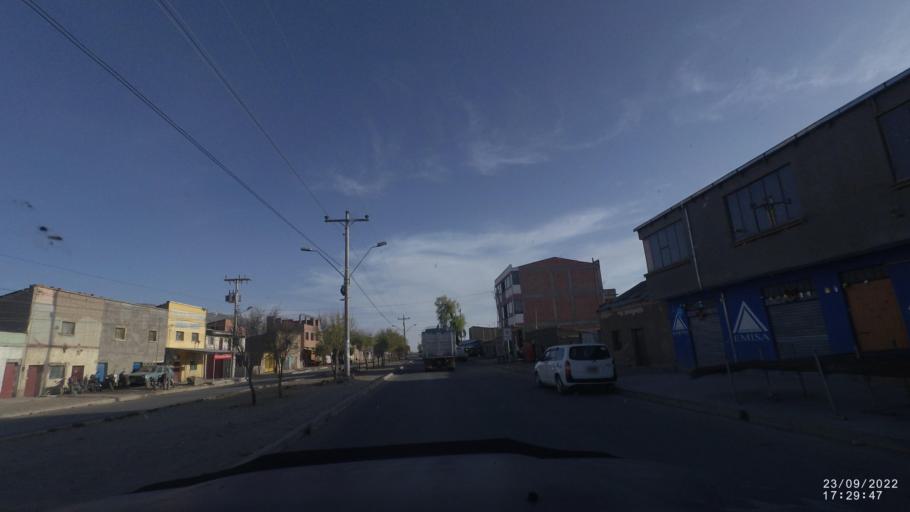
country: BO
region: Oruro
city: Challapata
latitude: -18.9050
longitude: -66.7771
